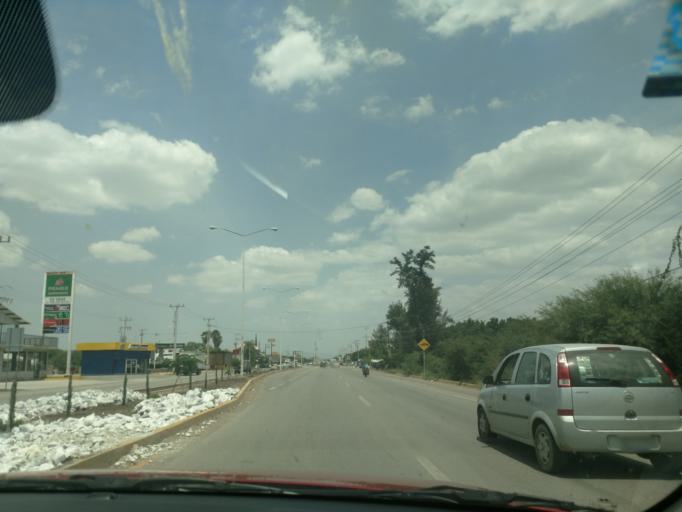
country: MX
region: San Luis Potosi
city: Ciudad Fernandez
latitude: 21.9376
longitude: -100.0314
